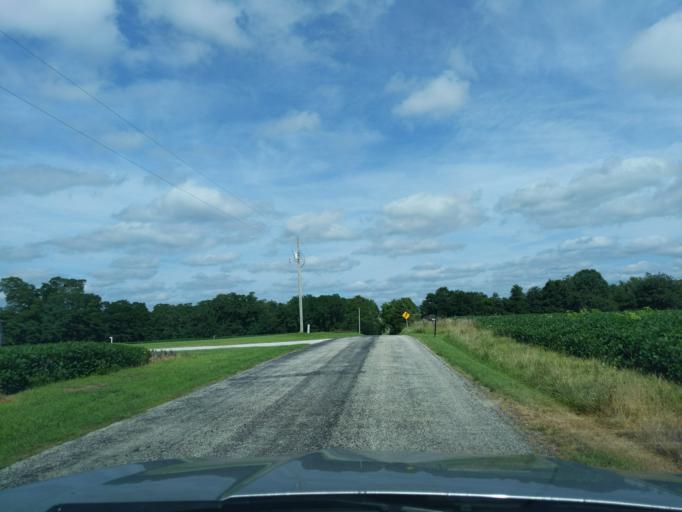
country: US
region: Indiana
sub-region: Ripley County
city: Osgood
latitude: 39.2349
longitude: -85.3830
